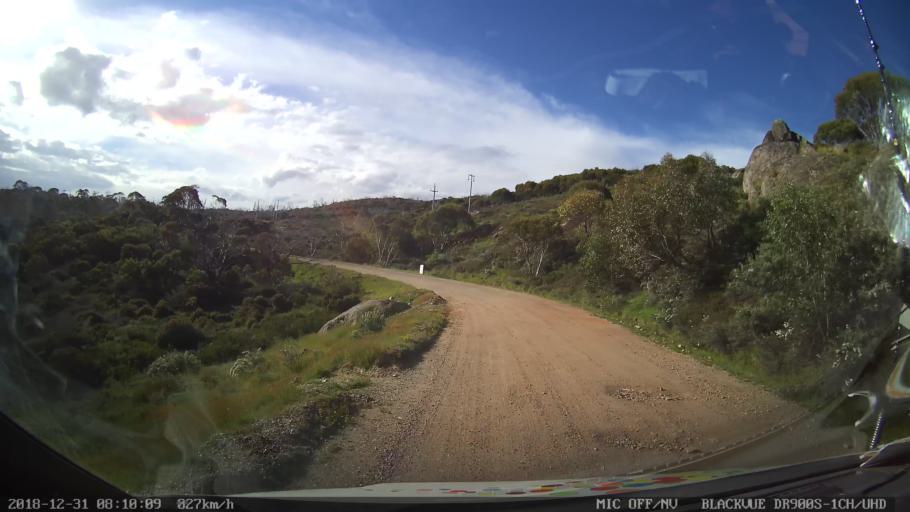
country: AU
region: New South Wales
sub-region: Snowy River
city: Jindabyne
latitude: -36.3821
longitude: 148.4204
